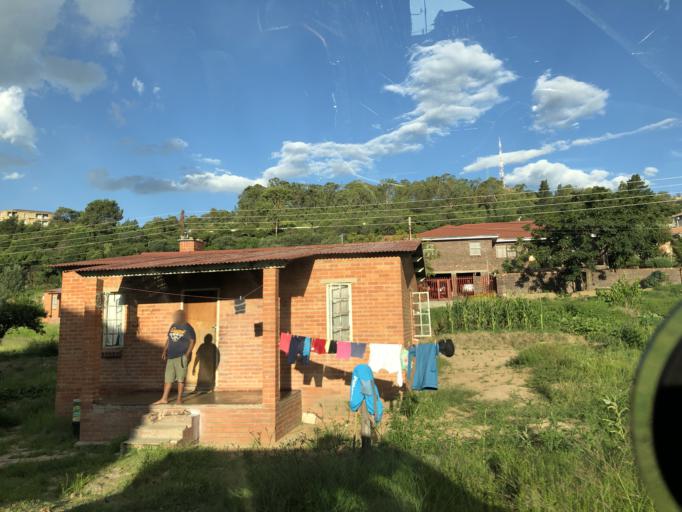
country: LS
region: Maseru
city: Maseru
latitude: -29.3201
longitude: 27.4865
